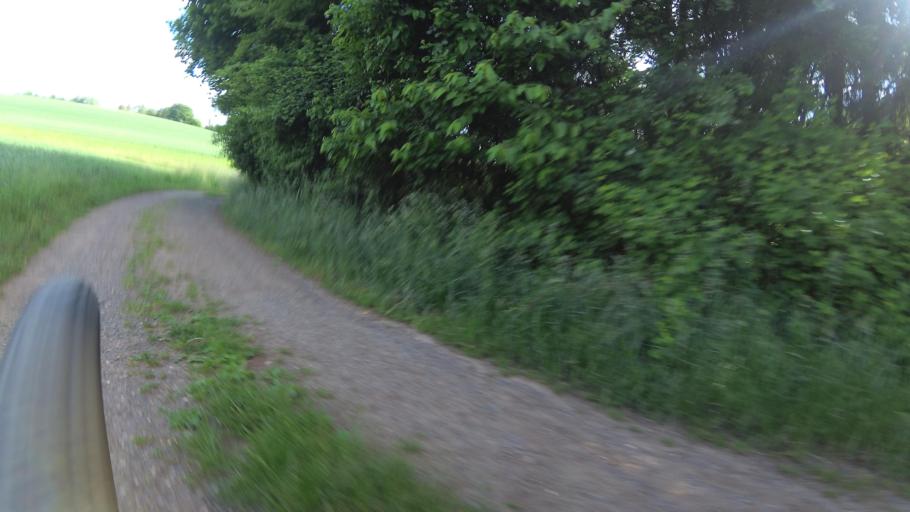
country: DE
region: Saarland
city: Heusweiler
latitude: 49.3250
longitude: 6.9283
